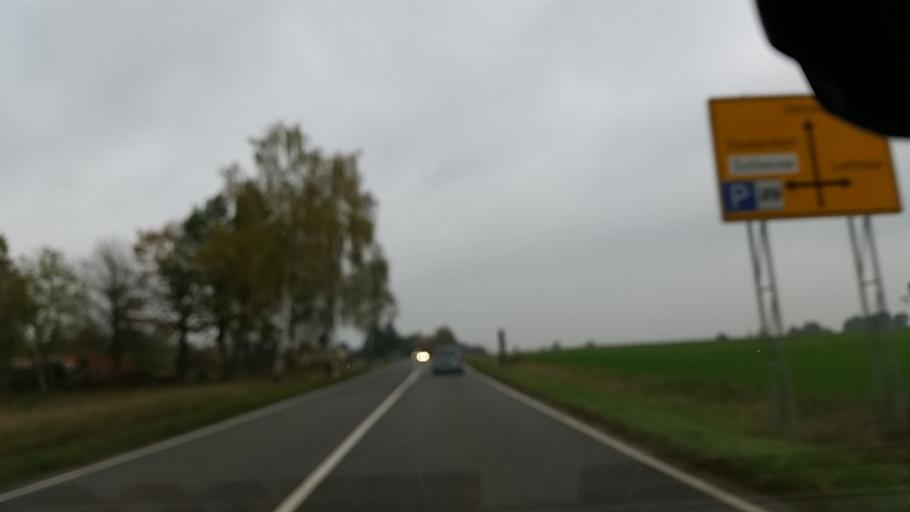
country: DE
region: Lower Saxony
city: Wrestedt
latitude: 52.9184
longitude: 10.6194
